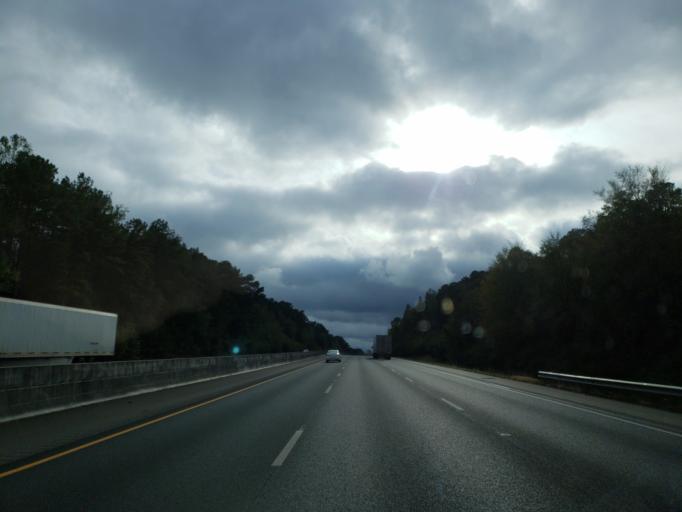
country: US
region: Alabama
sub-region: Bibb County
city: North Bibb
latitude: 33.2254
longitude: -87.1760
